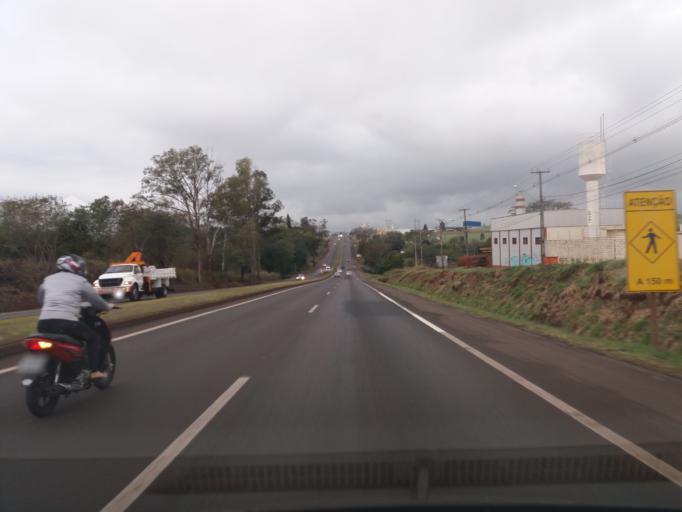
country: BR
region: Parana
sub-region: Sarandi
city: Sarandi
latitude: -23.4523
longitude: -51.8525
